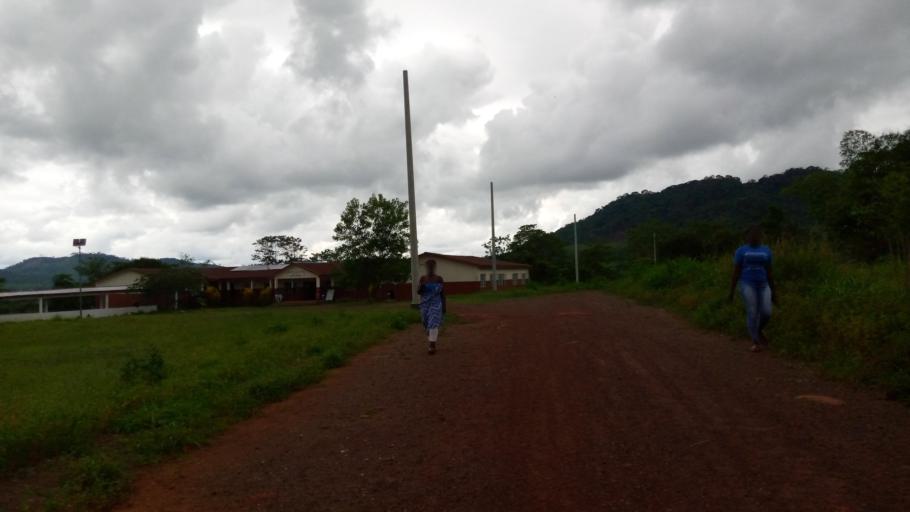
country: SL
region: Southern Province
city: Moyamba
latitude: 8.1589
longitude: -12.4444
